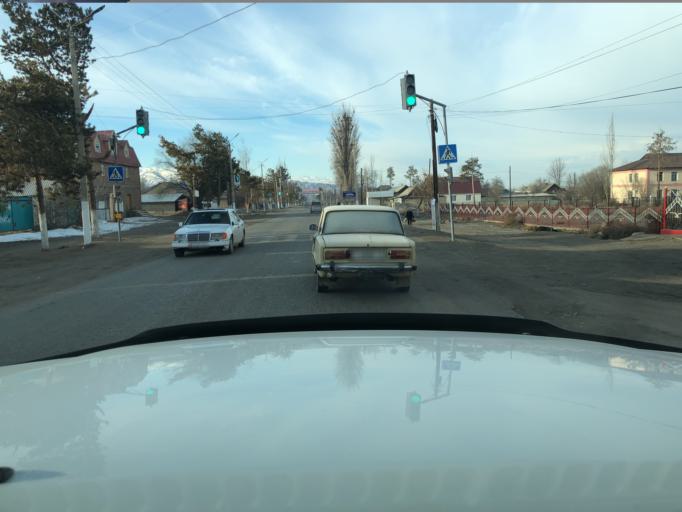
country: KG
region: Ysyk-Koel
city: Pokrovka
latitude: 42.3440
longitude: 78.0090
